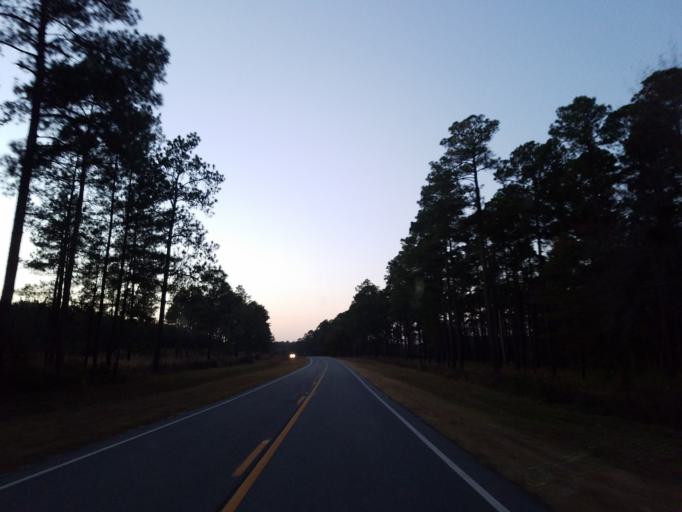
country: US
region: Georgia
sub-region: Wilcox County
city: Rochelle
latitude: 31.8214
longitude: -83.5425
